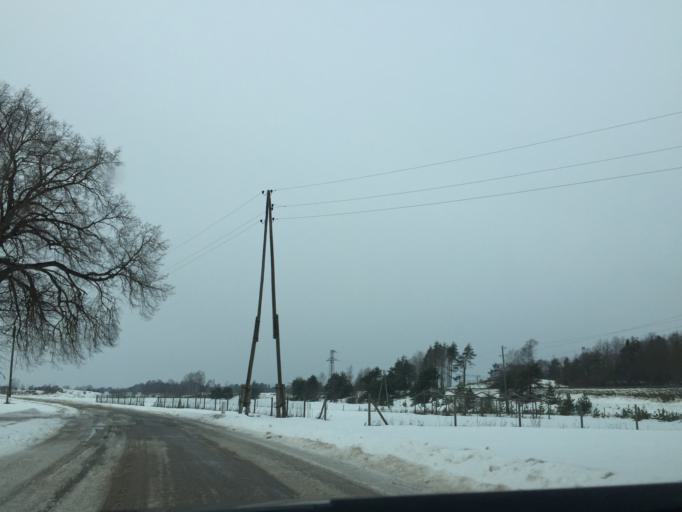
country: LV
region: Ikskile
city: Ikskile
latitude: 56.8447
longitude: 24.4692
